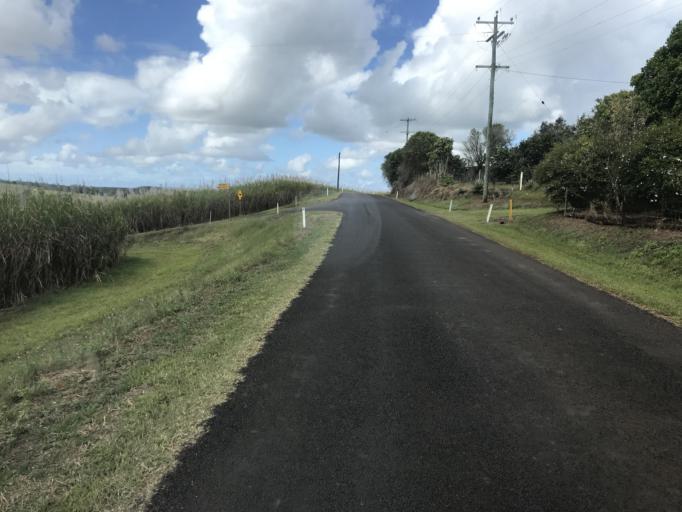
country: AU
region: Queensland
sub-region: Cassowary Coast
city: Innisfail
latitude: -17.5538
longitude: 145.8904
